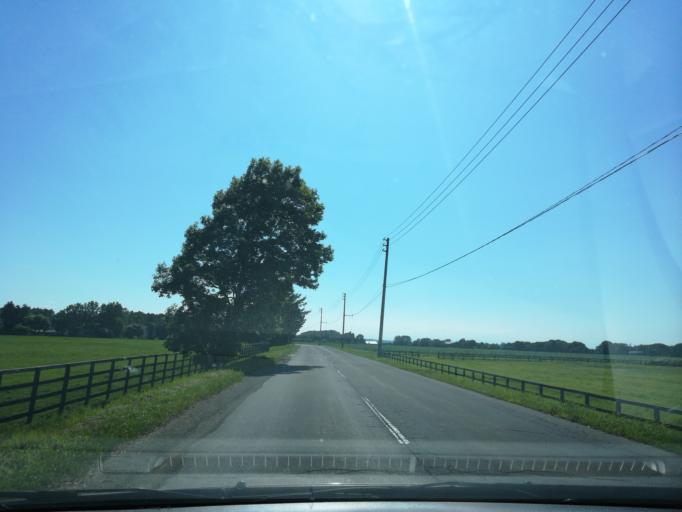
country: JP
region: Hokkaido
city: Chitose
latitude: 42.9217
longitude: 141.8711
